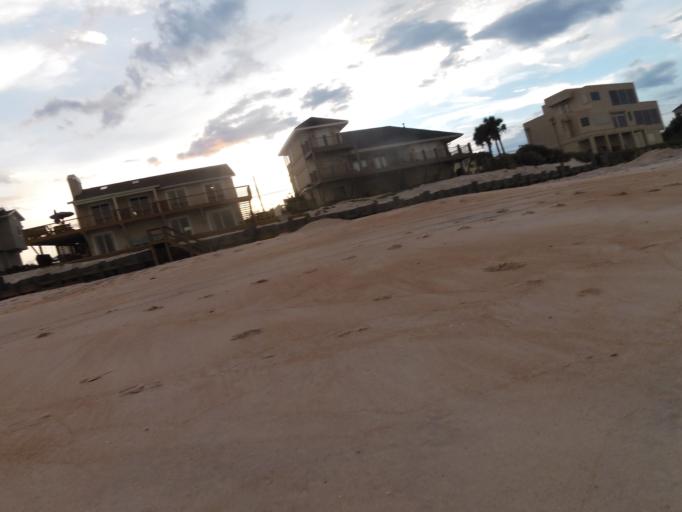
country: US
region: Florida
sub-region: Saint Johns County
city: Villano Beach
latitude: 29.9765
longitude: -81.3109
